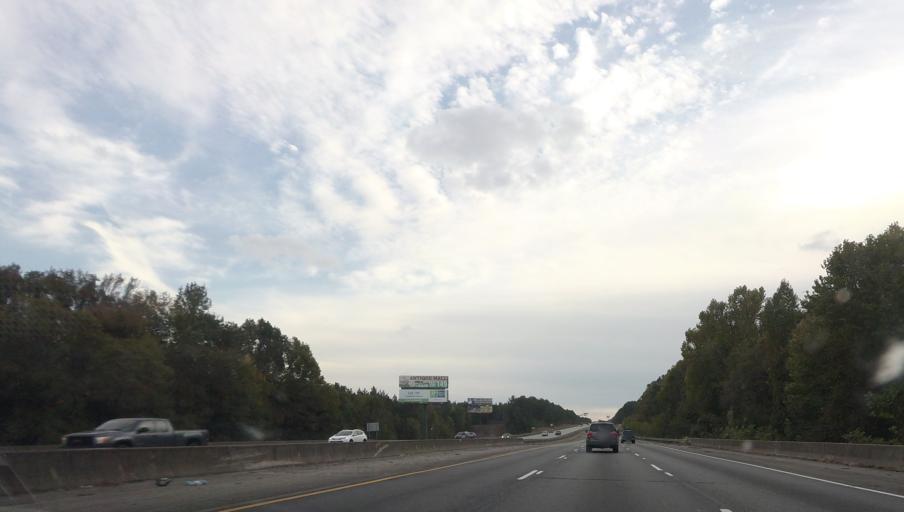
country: US
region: Georgia
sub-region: Peach County
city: Byron
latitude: 32.6944
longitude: -83.7376
